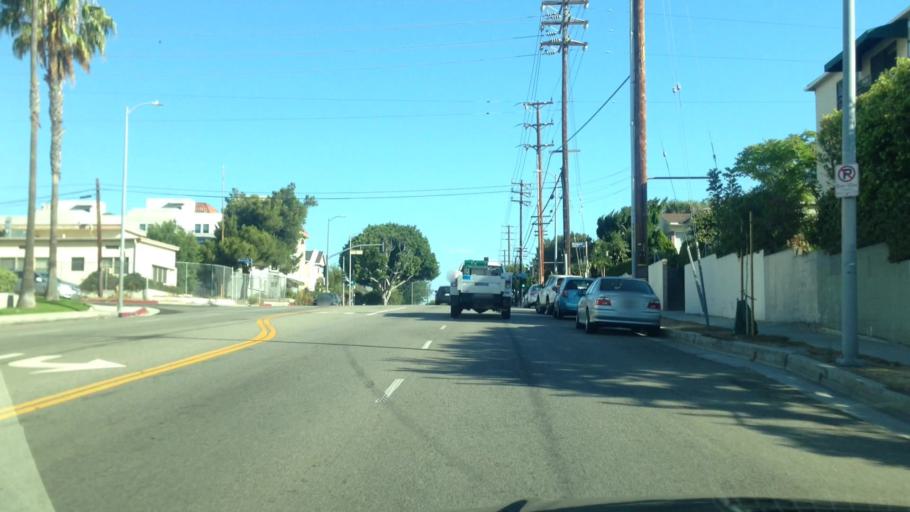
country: US
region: California
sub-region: Los Angeles County
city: Marina del Rey
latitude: 34.0069
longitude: -118.4360
